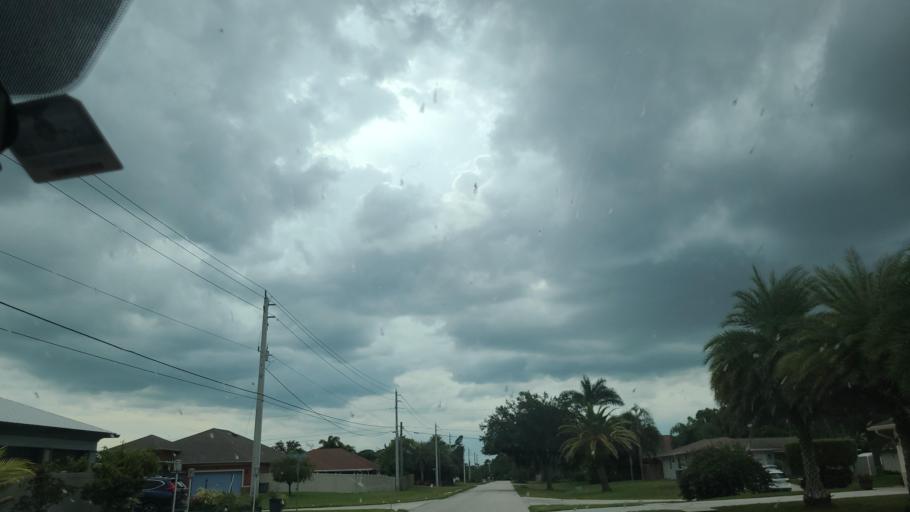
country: US
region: Florida
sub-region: Saint Lucie County
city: Port Saint Lucie
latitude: 27.2480
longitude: -80.4035
